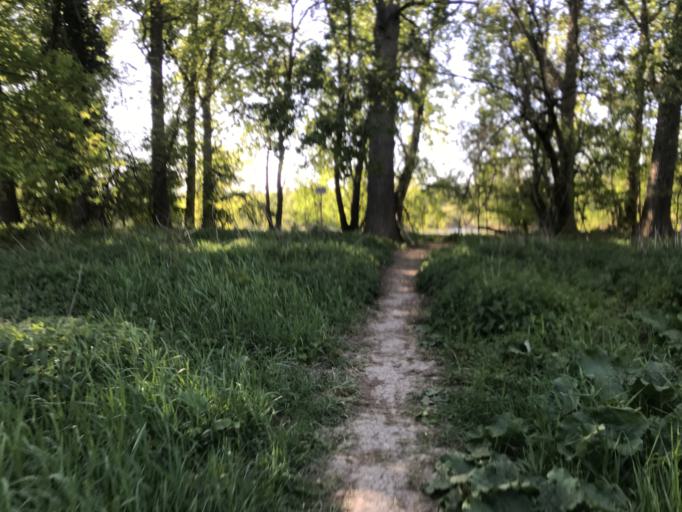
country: DE
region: Hesse
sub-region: Regierungsbezirk Darmstadt
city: Eltville
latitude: 50.0197
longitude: 8.1392
